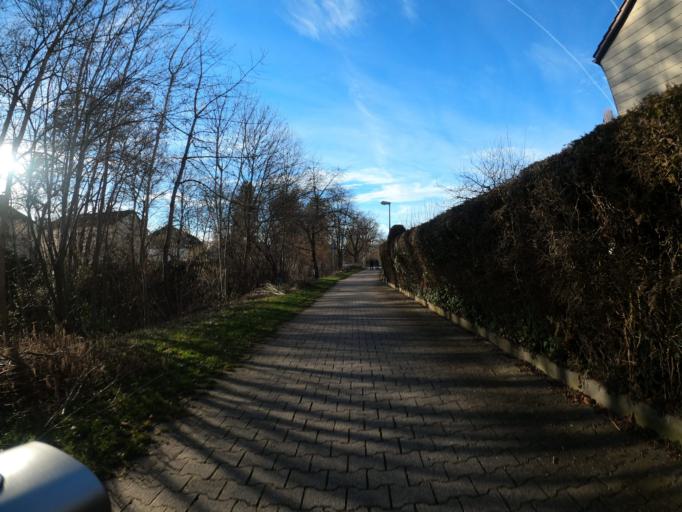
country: DE
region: Baden-Wuerttemberg
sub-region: Regierungsbezirk Stuttgart
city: Wernau
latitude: 48.6604
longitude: 9.4158
